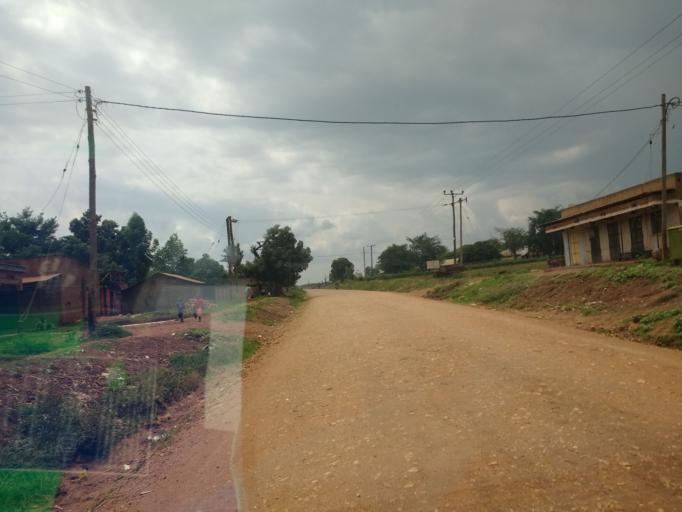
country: UG
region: Eastern Region
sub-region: Sironko District
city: Sironko
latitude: 1.3388
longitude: 34.2992
